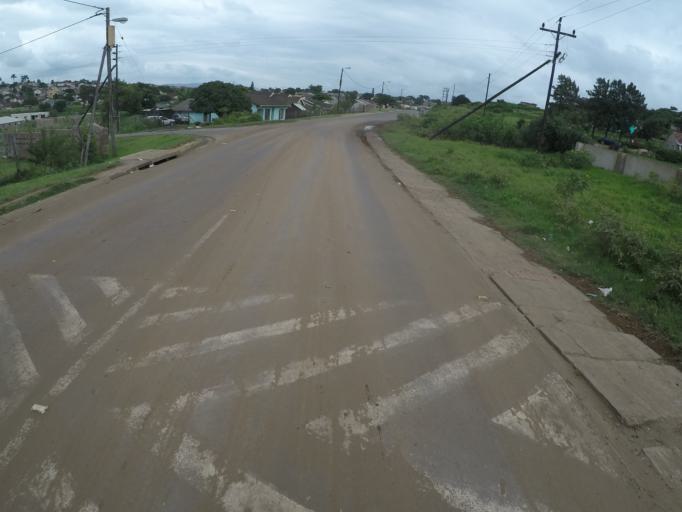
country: ZA
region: KwaZulu-Natal
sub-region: uThungulu District Municipality
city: Empangeni
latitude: -28.7727
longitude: 31.8536
